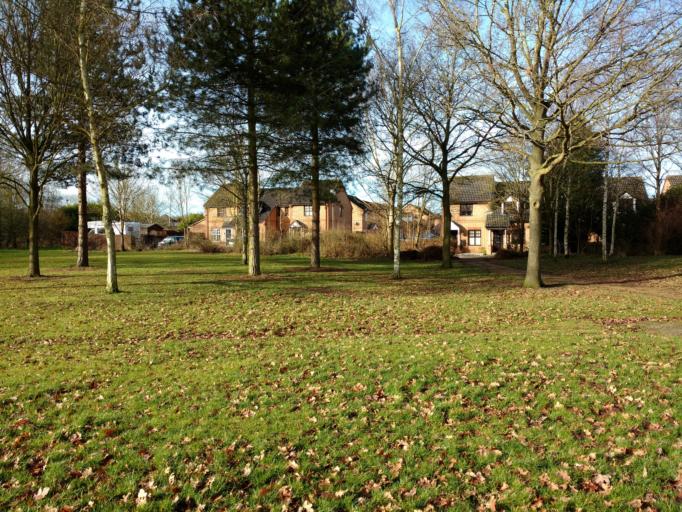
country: GB
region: England
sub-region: Buckinghamshire
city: Newton Longville
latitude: 52.0006
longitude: -0.7761
